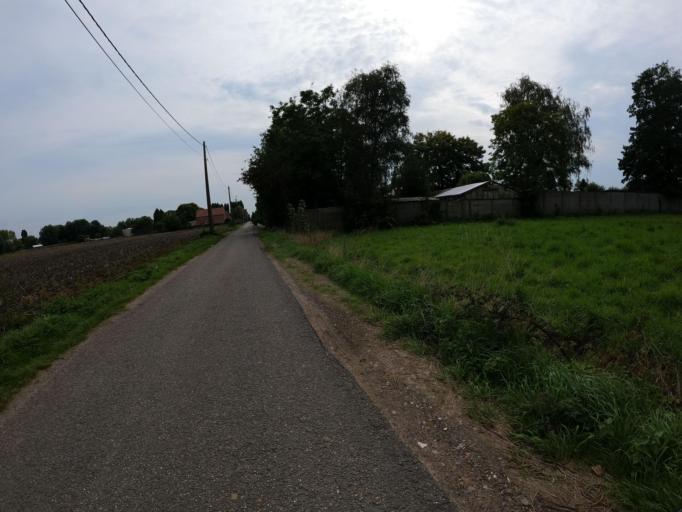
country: BE
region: Flanders
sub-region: Provincie Antwerpen
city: Wommelgem
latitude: 51.1996
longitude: 4.5100
